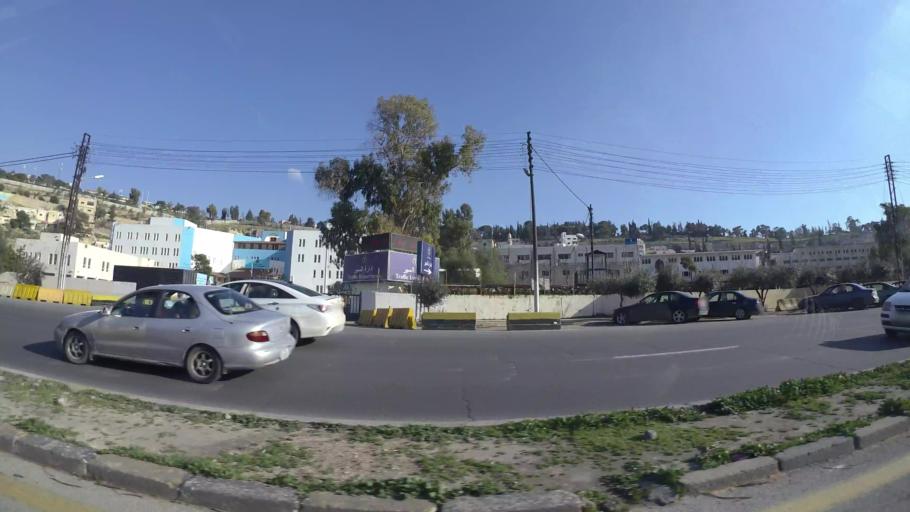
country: JO
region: Amman
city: Amman
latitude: 31.9709
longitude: 35.9695
